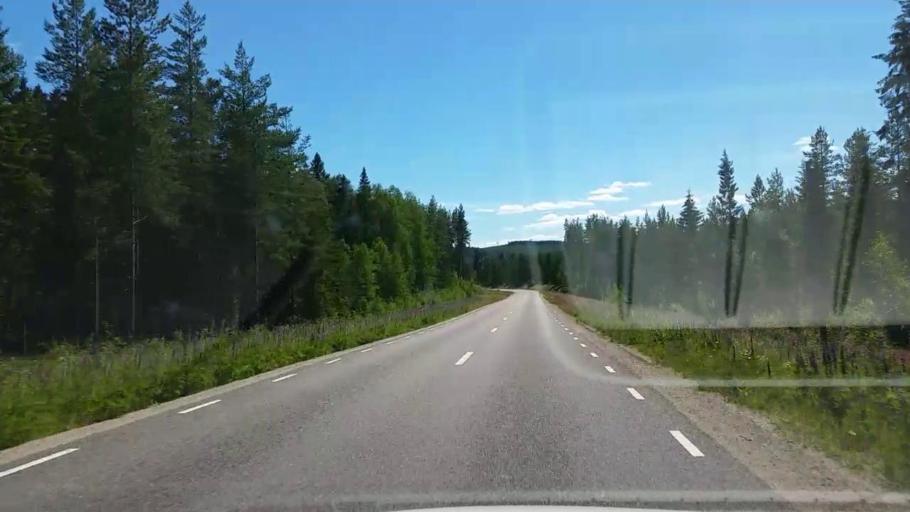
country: SE
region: Gaevleborg
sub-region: Ovanakers Kommun
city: Edsbyn
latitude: 61.4313
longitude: 15.7201
